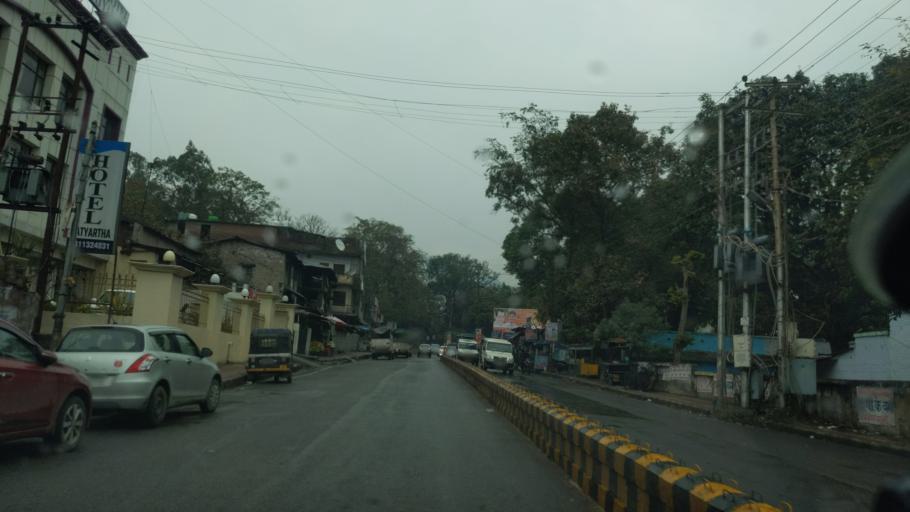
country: IN
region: Uttarakhand
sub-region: Naini Tal
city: Haldwani
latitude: 29.2645
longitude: 79.5445
